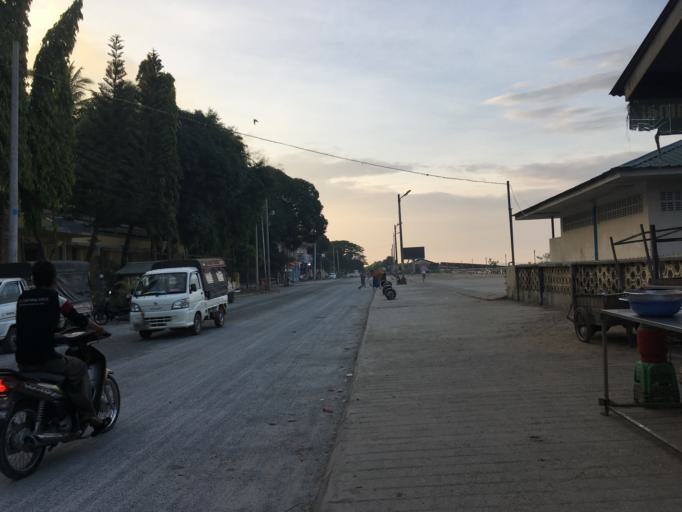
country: MM
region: Mon
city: Mawlamyine
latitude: 16.4832
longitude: 97.6185
